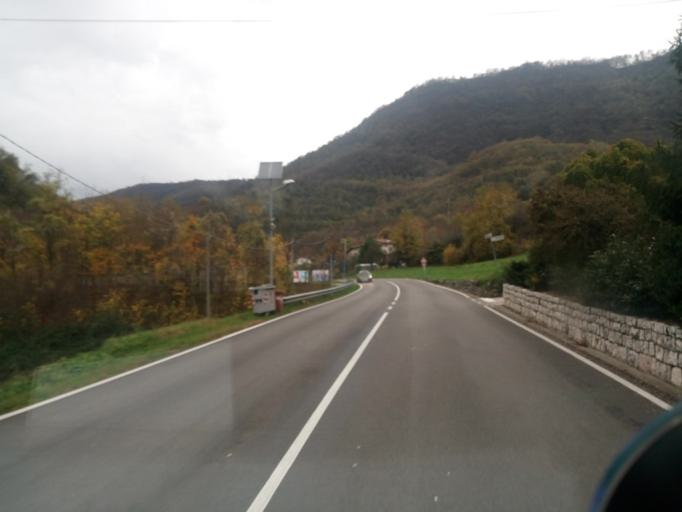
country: IT
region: Veneto
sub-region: Provincia di Vicenza
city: Monte di Malo
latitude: 45.6392
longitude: 11.3757
